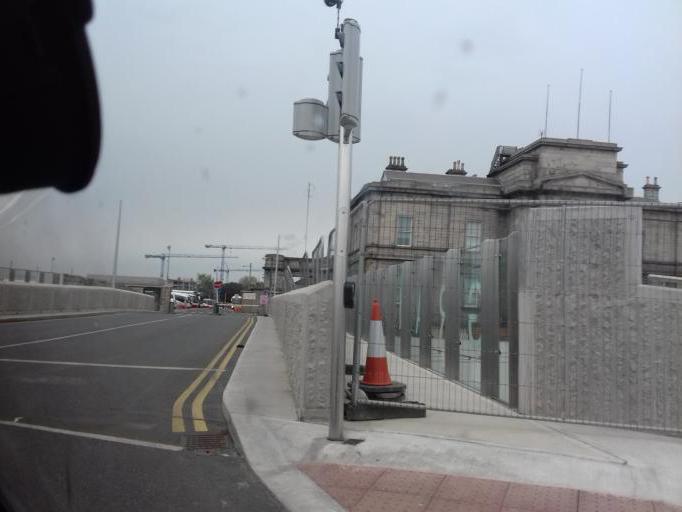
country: IE
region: Leinster
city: Cabra
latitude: 53.3537
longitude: -6.2741
